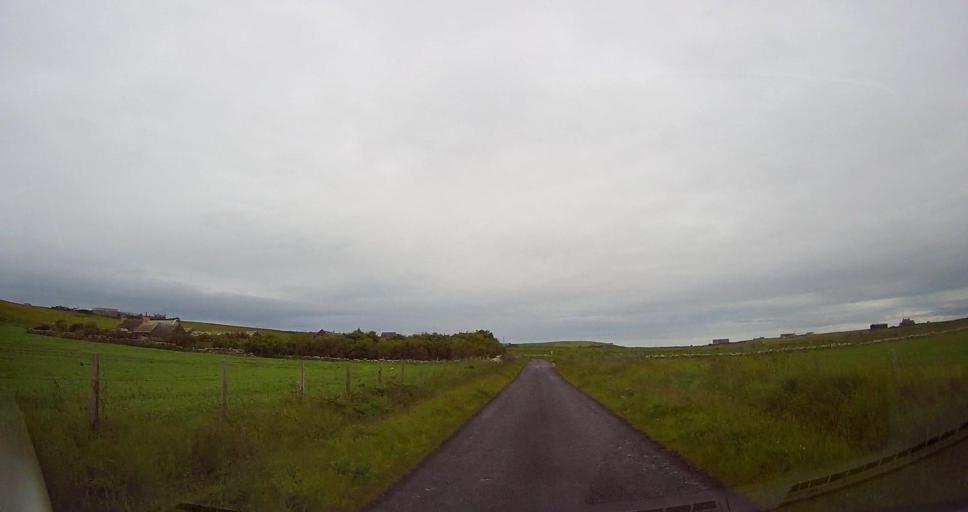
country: GB
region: Scotland
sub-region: Orkney Islands
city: Stromness
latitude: 59.1264
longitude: -3.2896
